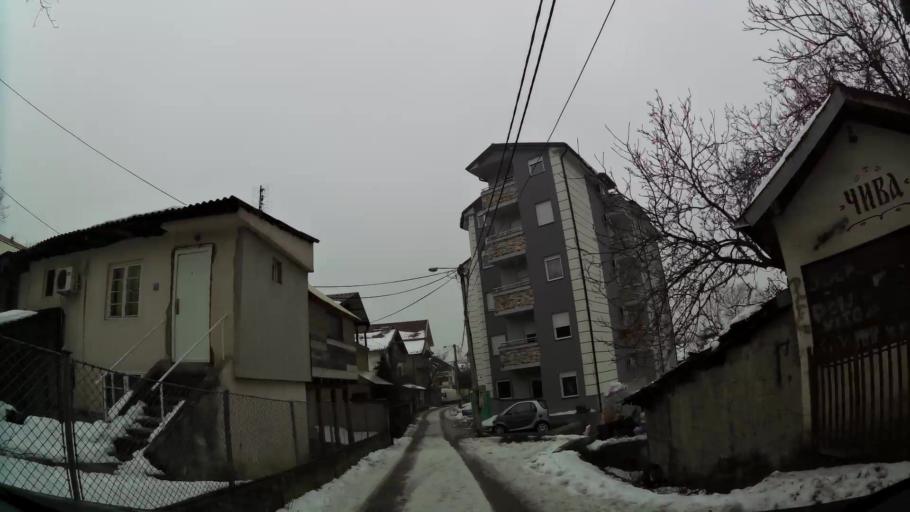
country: RS
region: Central Serbia
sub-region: Belgrade
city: Zvezdara
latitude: 44.7817
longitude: 20.5160
